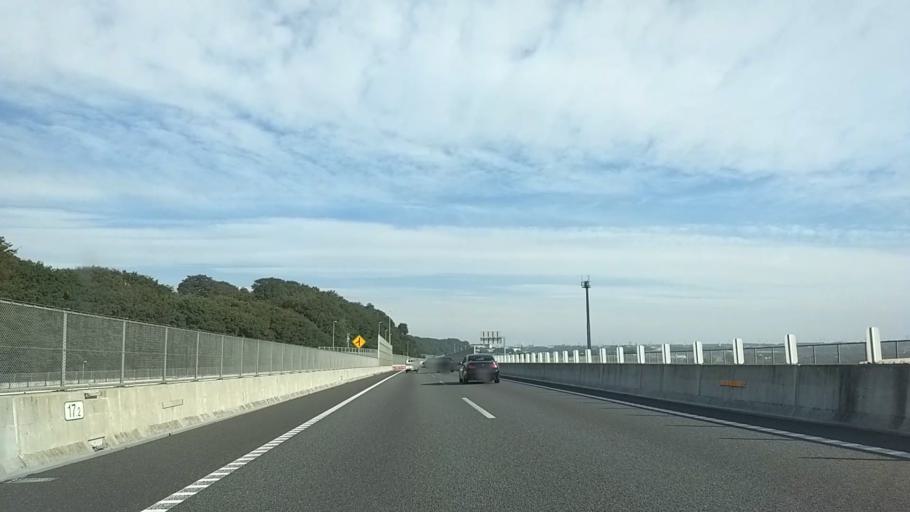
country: JP
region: Kanagawa
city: Zama
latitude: 35.4892
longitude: 139.3694
